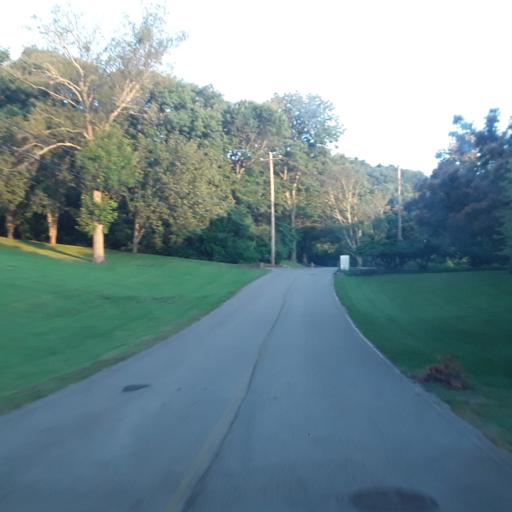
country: US
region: Tennessee
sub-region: Davidson County
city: Oak Hill
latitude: 36.0702
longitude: -86.7807
